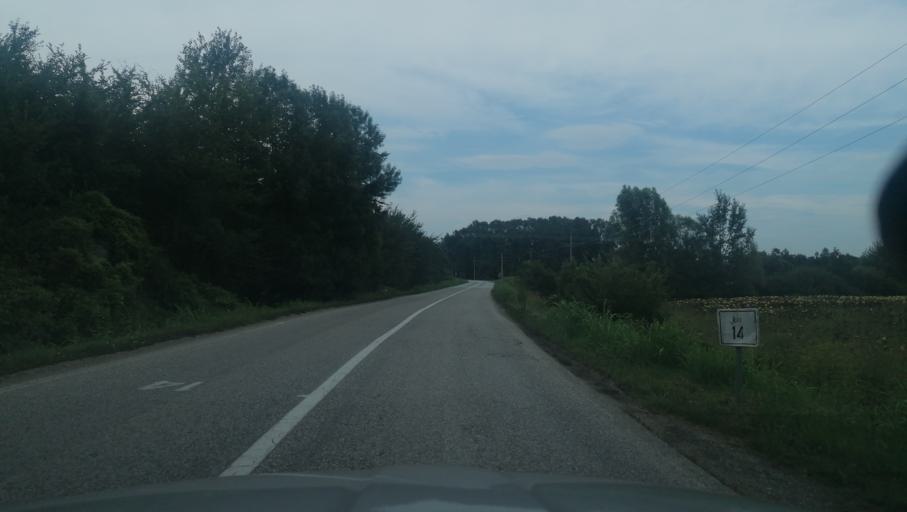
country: RS
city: Glusci
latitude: 44.9218
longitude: 19.5429
